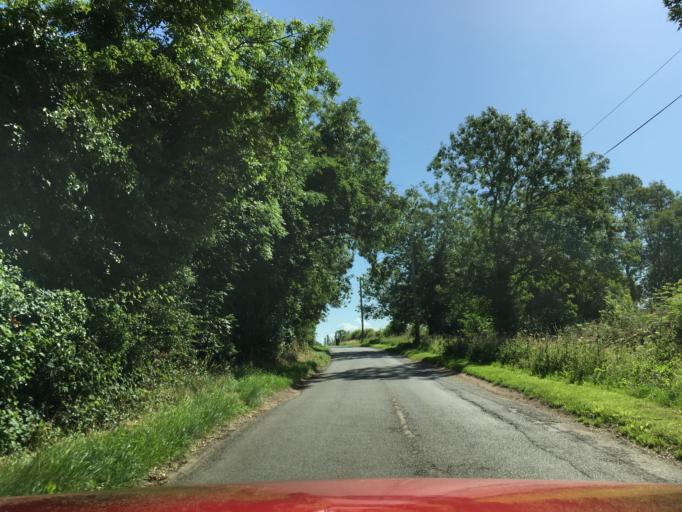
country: GB
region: England
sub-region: Buckinghamshire
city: Winslow
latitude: 51.9945
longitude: -0.8940
